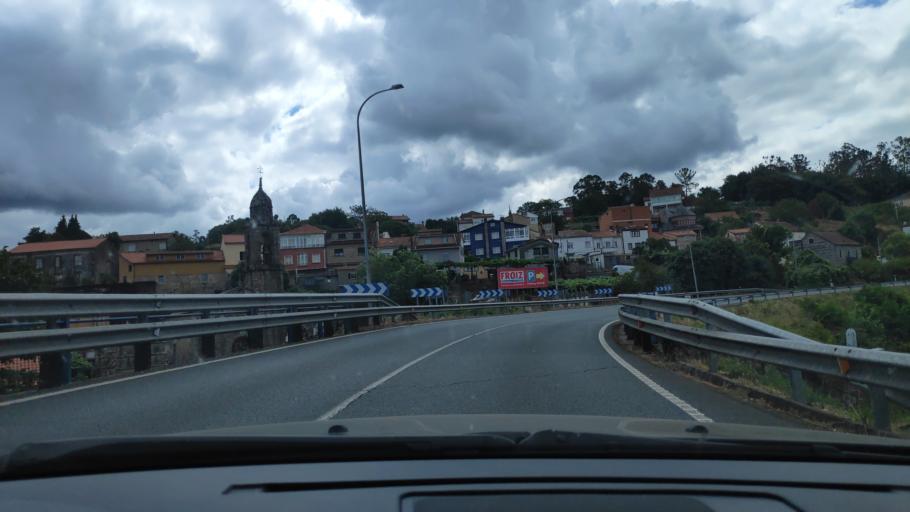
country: ES
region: Galicia
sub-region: Provincia da Coruna
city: Padron
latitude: 42.7254
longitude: -8.6514
